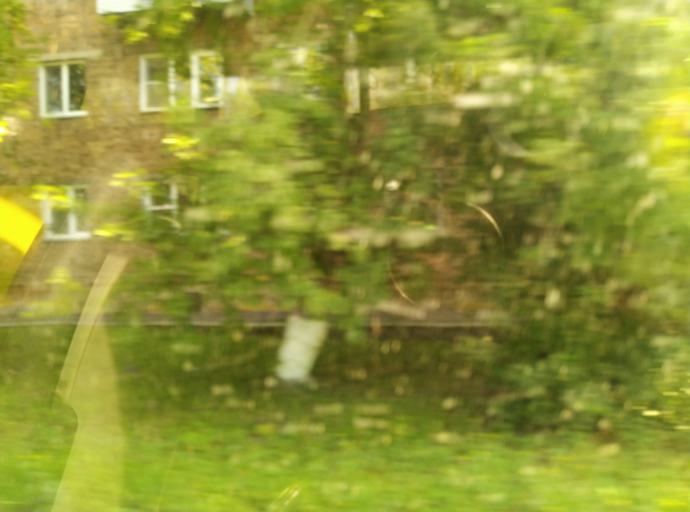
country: RU
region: Krasnoyarskiy
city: Krasnoyarsk
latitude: 55.9782
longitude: 92.8425
